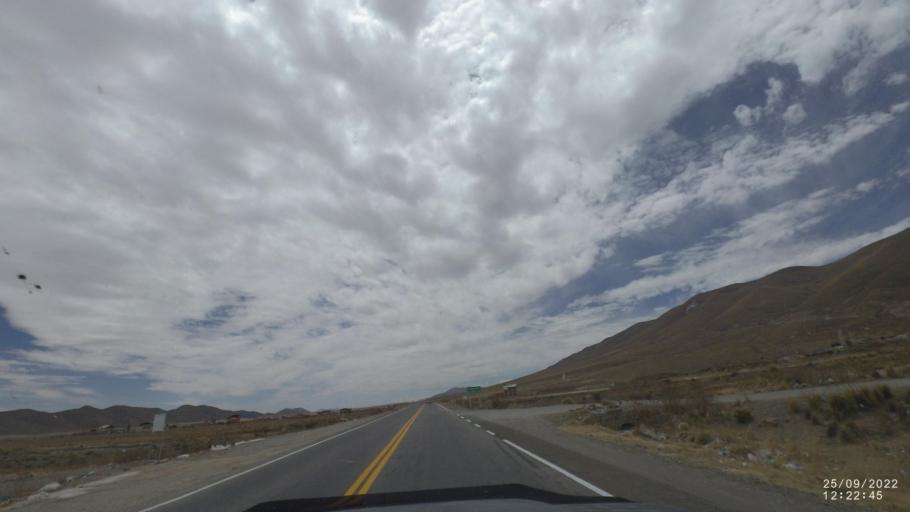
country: BO
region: Oruro
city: Poopo
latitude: -18.3857
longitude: -66.9789
